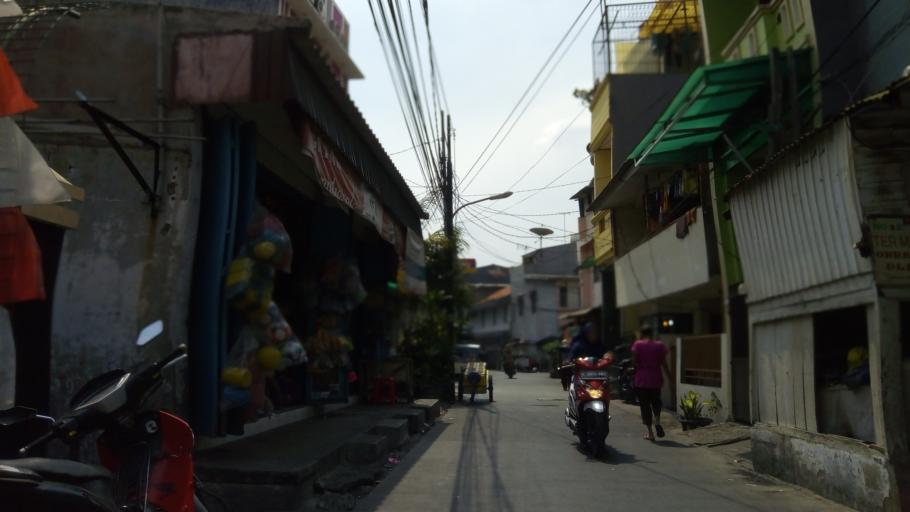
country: ID
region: Jakarta Raya
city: Jakarta
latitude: -6.1535
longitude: 106.8320
